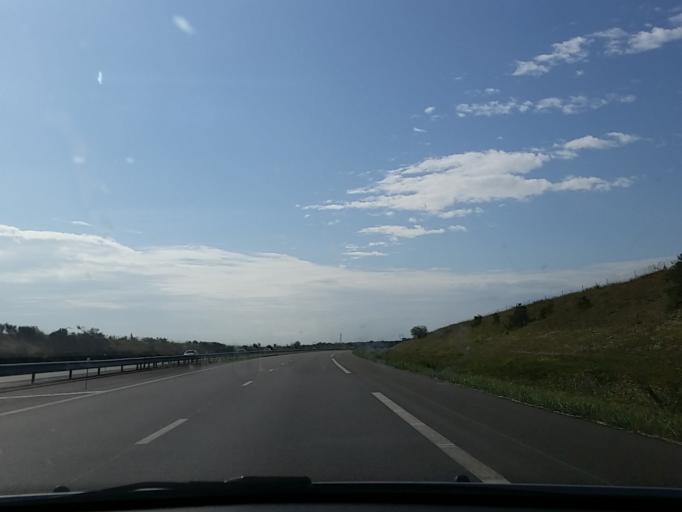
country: FR
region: Centre
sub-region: Departement du Cher
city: Trouy
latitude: 46.9983
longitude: 2.4052
